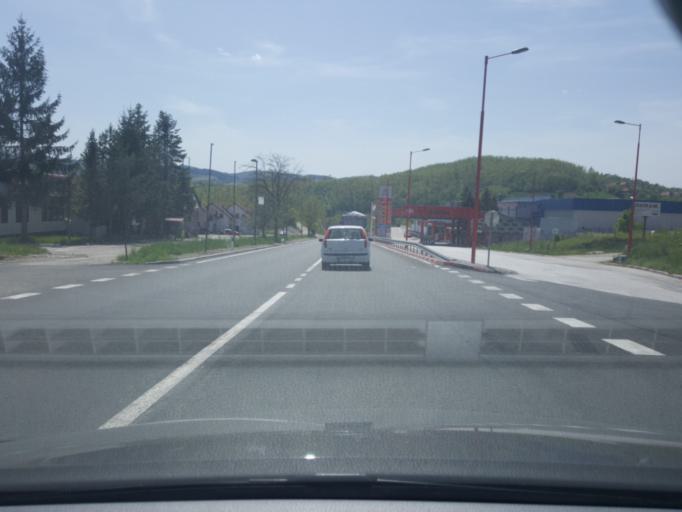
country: RS
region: Central Serbia
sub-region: Zlatiborski Okrug
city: Cajetina
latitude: 43.7919
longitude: 19.7606
